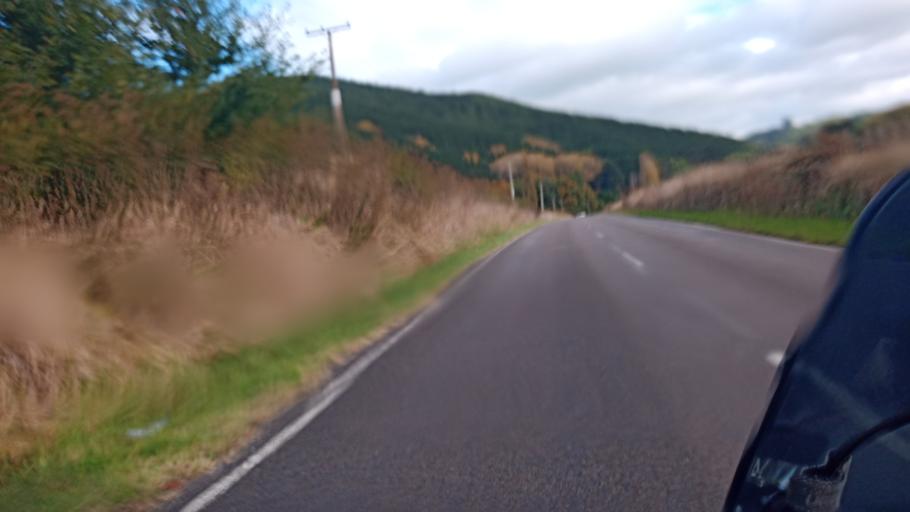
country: NZ
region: Gisborne
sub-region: Gisborne District
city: Gisborne
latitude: -38.5710
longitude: 177.7280
